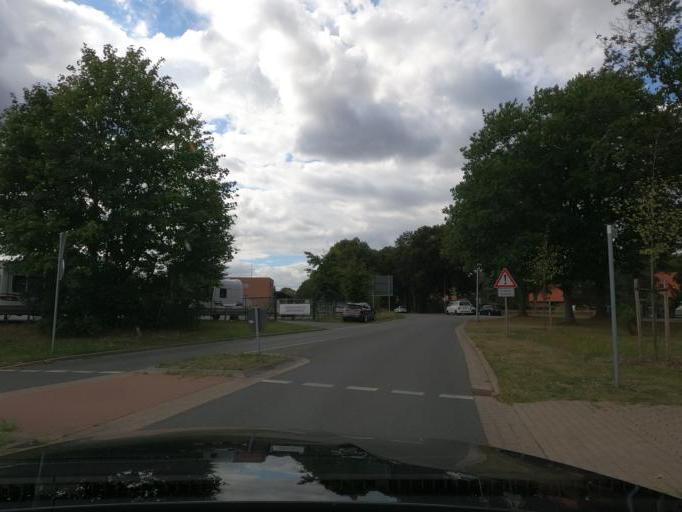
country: DE
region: Lower Saxony
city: Isernhagen Farster Bauerschaft
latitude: 52.4411
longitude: 9.8901
